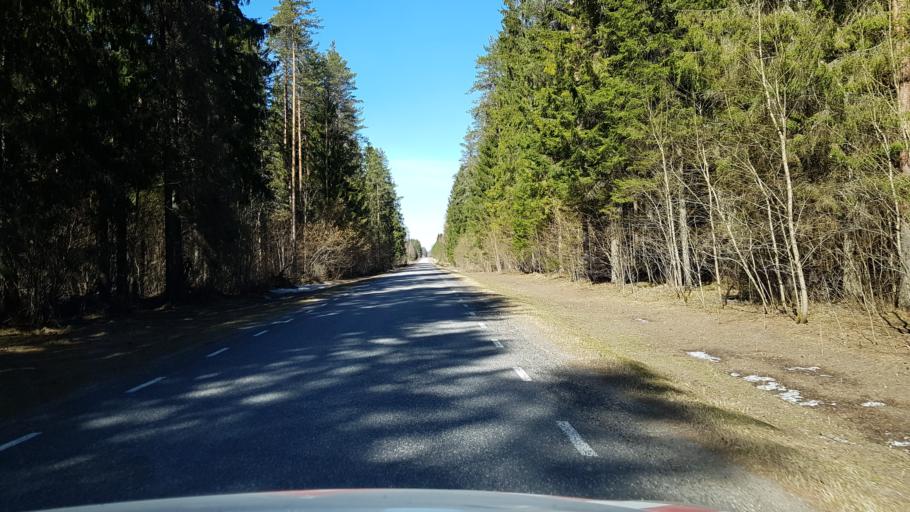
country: EE
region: Laeaene-Virumaa
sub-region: Vinni vald
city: Vinni
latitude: 59.1536
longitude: 26.5170
